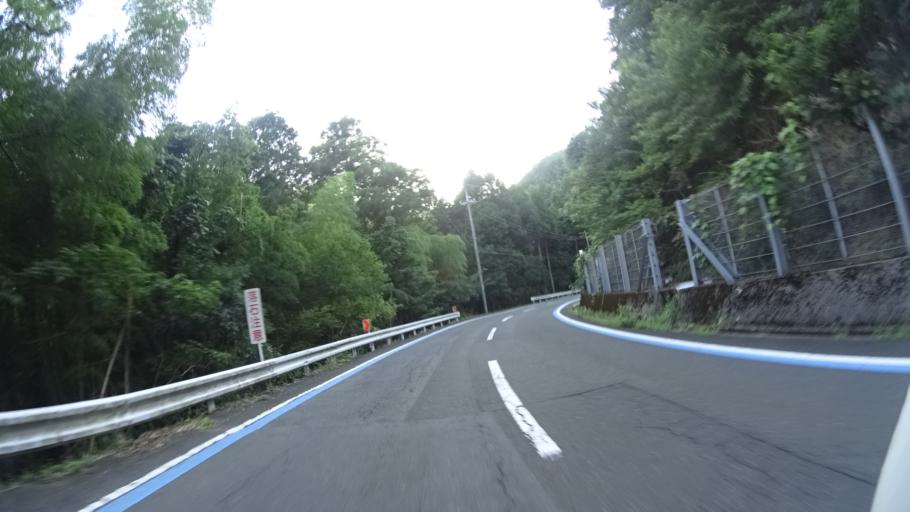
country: JP
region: Kyoto
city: Maizuru
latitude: 35.4418
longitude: 135.3948
